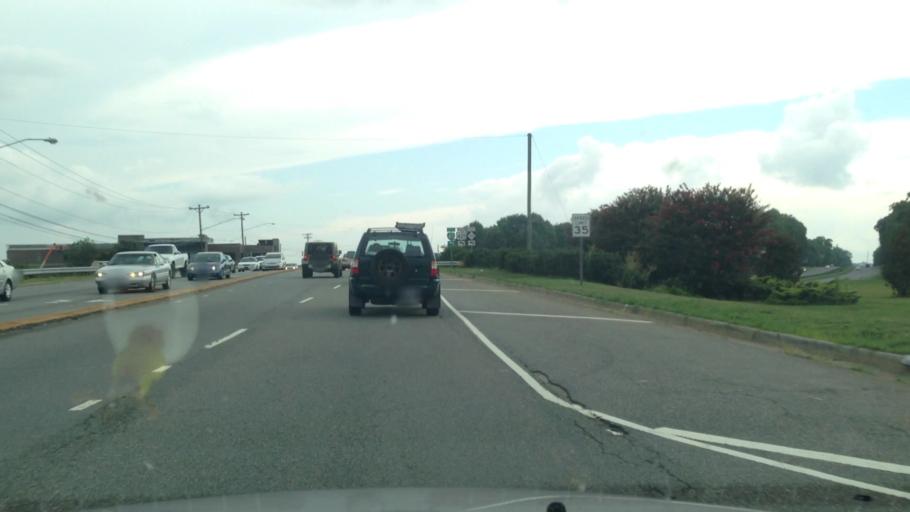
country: US
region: North Carolina
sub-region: Forsyth County
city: Kernersville
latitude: 36.1108
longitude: -80.0901
